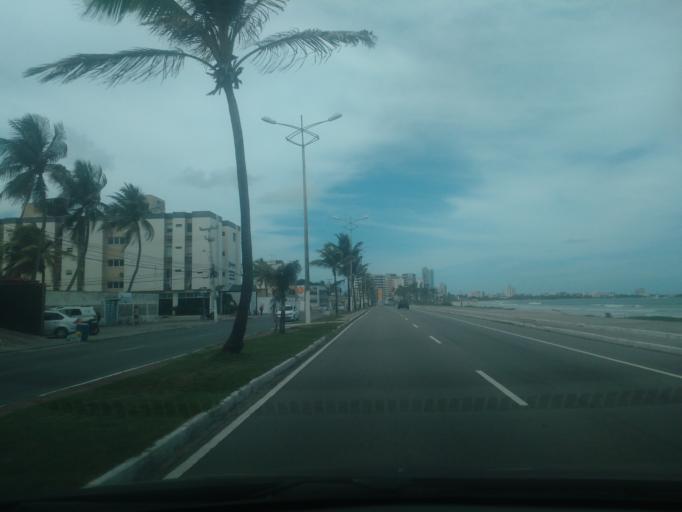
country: BR
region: Alagoas
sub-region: Maceio
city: Maceio
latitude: -9.6722
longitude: -35.7459
